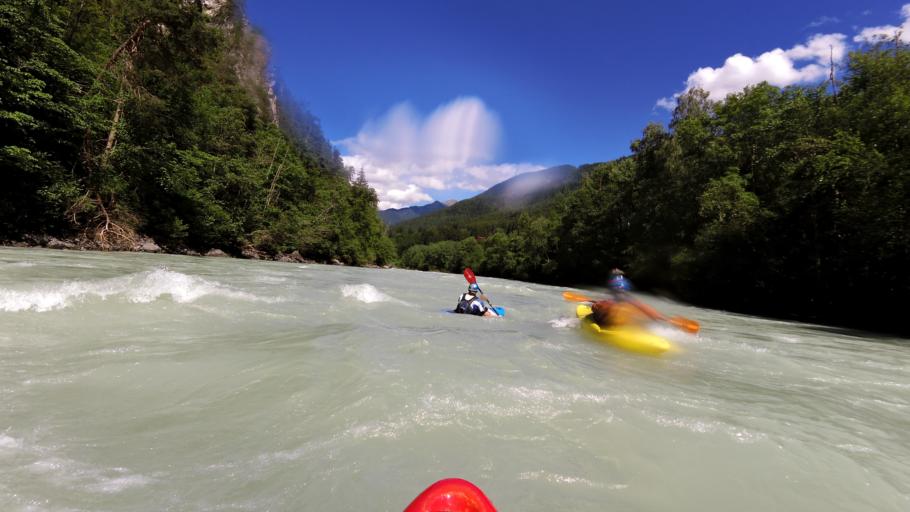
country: AT
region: Tyrol
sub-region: Politischer Bezirk Imst
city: Karres
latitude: 47.2109
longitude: 10.7933
